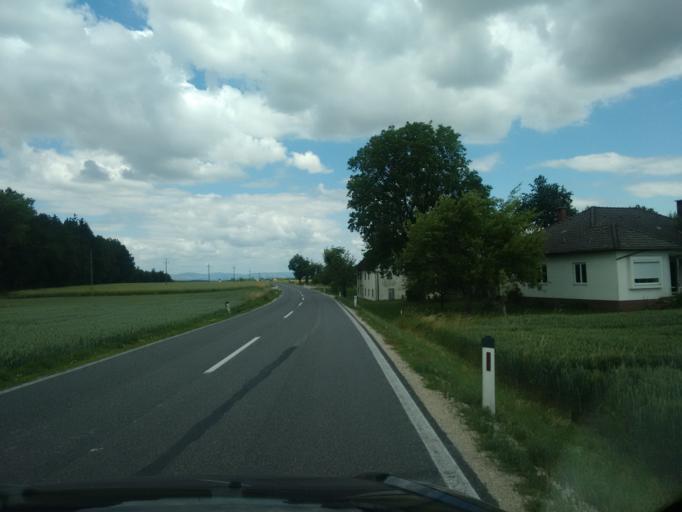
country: AT
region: Upper Austria
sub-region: Politischer Bezirk Steyr-Land
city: Sierning
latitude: 48.0926
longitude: 14.3188
